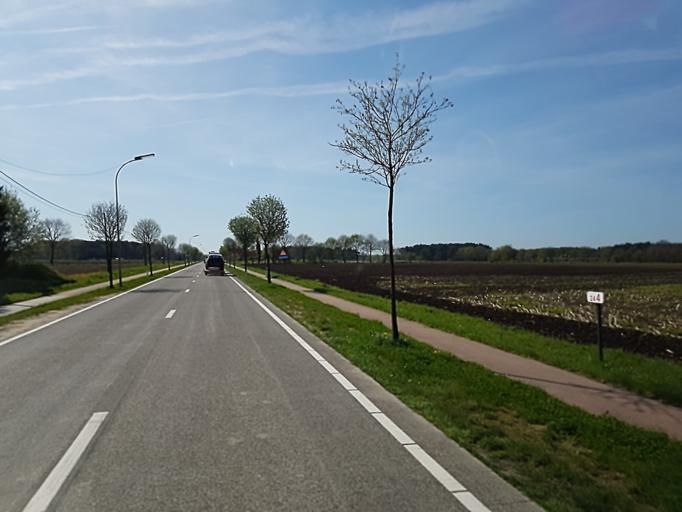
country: BE
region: Flanders
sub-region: Provincie Antwerpen
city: Westerlo
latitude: 51.1156
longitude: 4.9433
